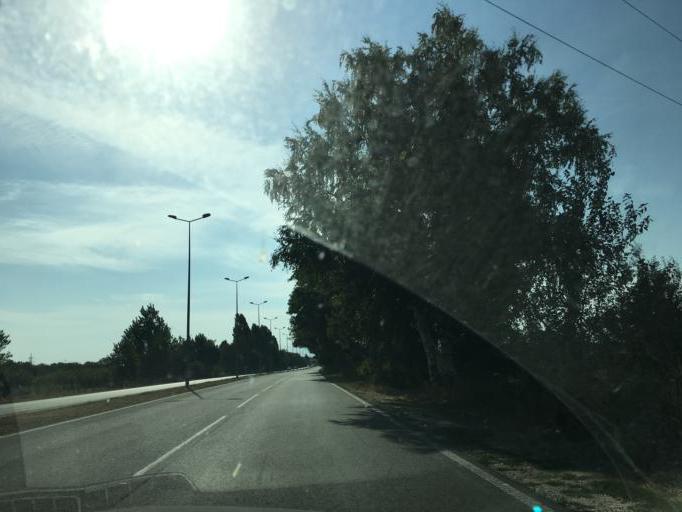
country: BG
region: Pazardzhik
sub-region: Obshtina Pazardzhik
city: Pazardzhik
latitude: 42.2175
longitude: 24.3165
